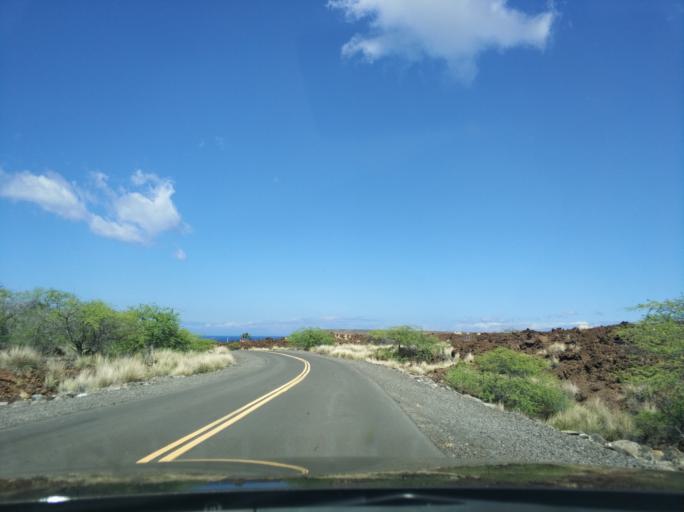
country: US
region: Hawaii
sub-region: Hawaii County
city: Kalaoa
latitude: 19.7987
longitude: -156.0075
